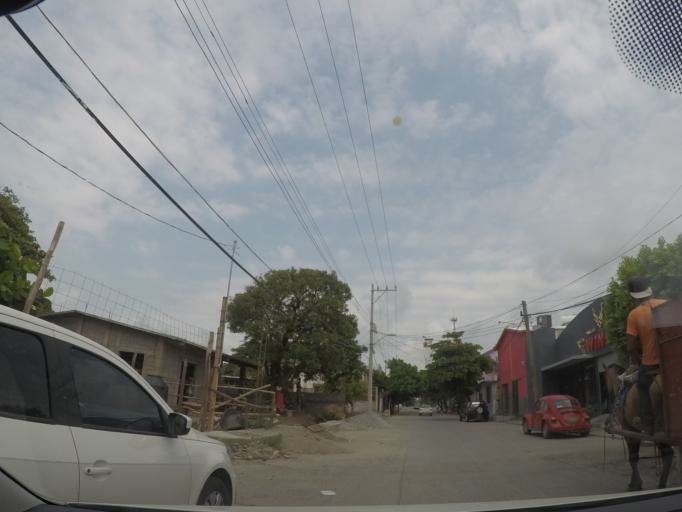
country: MX
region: Oaxaca
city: Juchitan de Zaragoza
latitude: 16.4421
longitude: -95.0185
